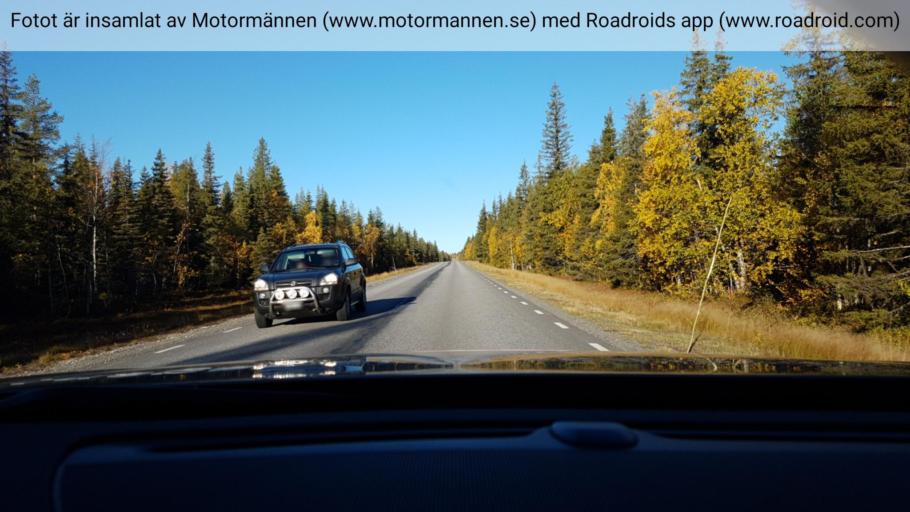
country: SE
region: Vaesterbotten
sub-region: Skelleftea Kommun
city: Storvik
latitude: 65.3547
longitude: 20.4725
